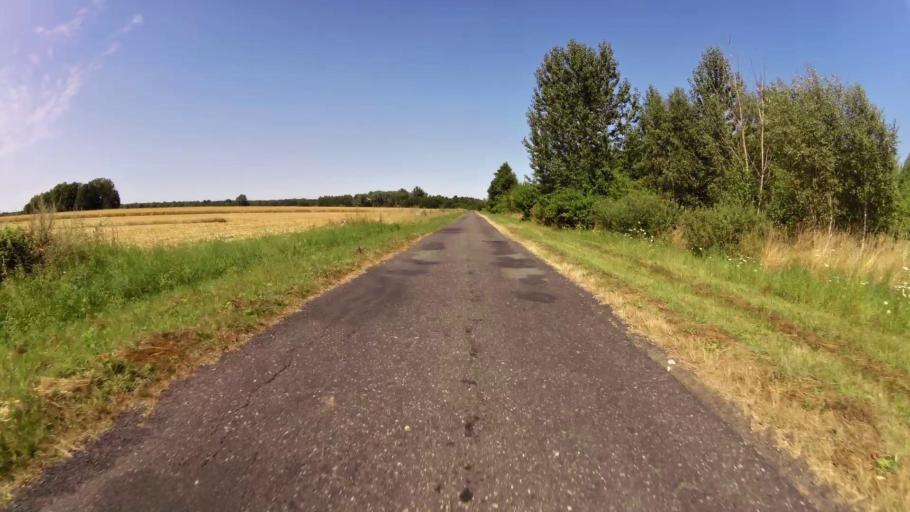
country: PL
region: West Pomeranian Voivodeship
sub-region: Powiat stargardzki
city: Suchan
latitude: 53.2848
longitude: 15.3627
